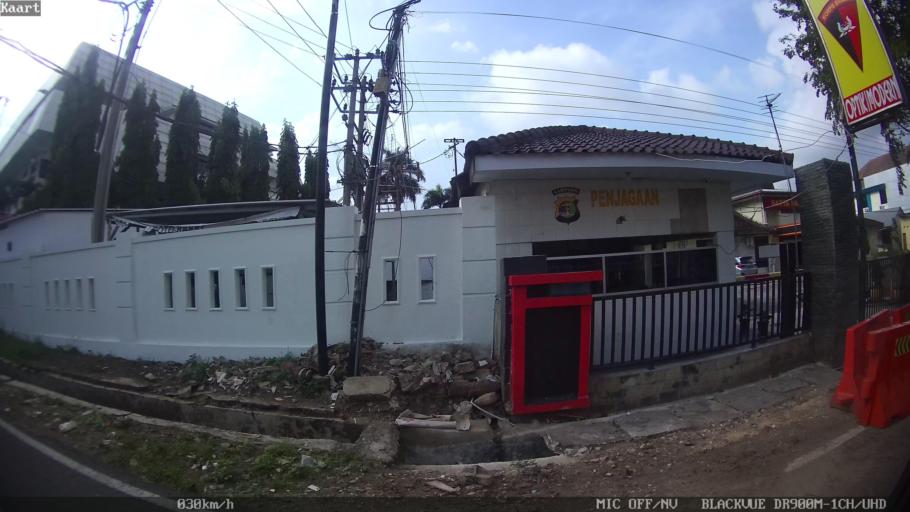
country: ID
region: Lampung
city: Bandarlampung
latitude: -5.4400
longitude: 105.2576
